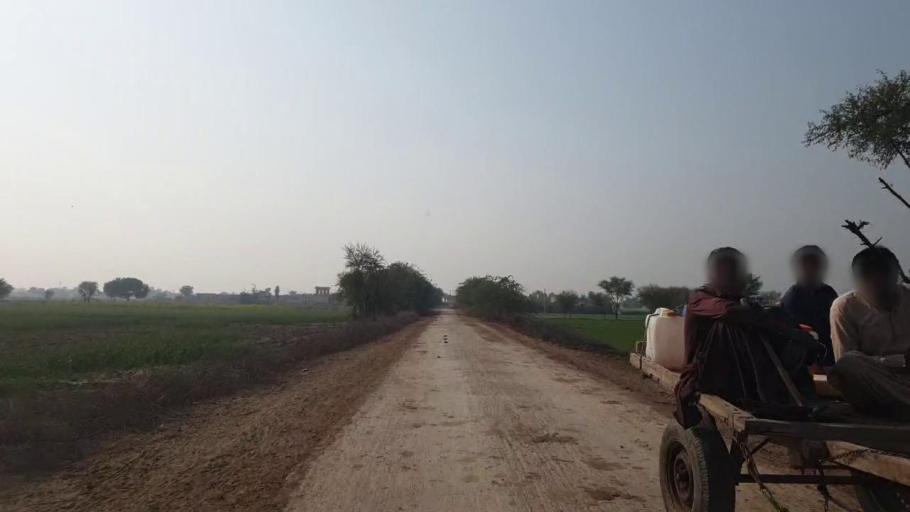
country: PK
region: Sindh
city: Shahdadpur
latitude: 26.0005
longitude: 68.5419
